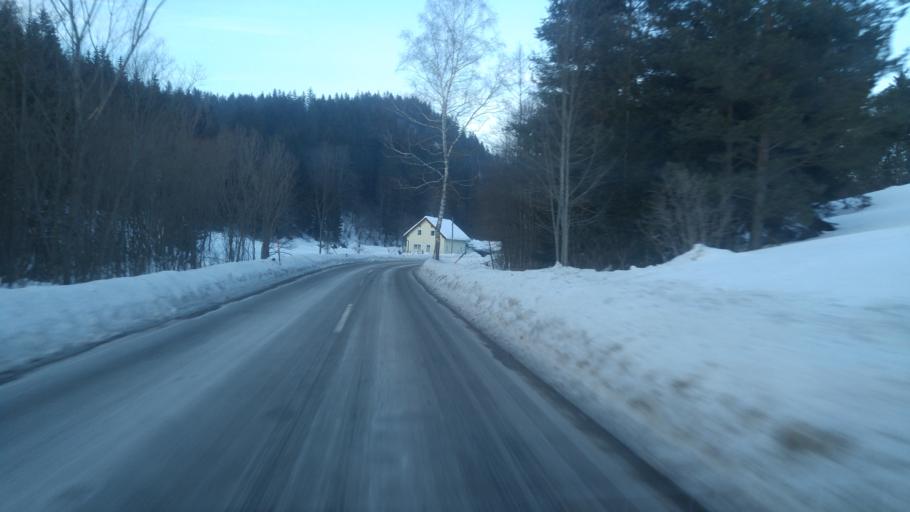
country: AT
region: Lower Austria
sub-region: Politischer Bezirk Wiener Neustadt
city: Rohr im Gebirge
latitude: 47.8752
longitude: 15.7053
